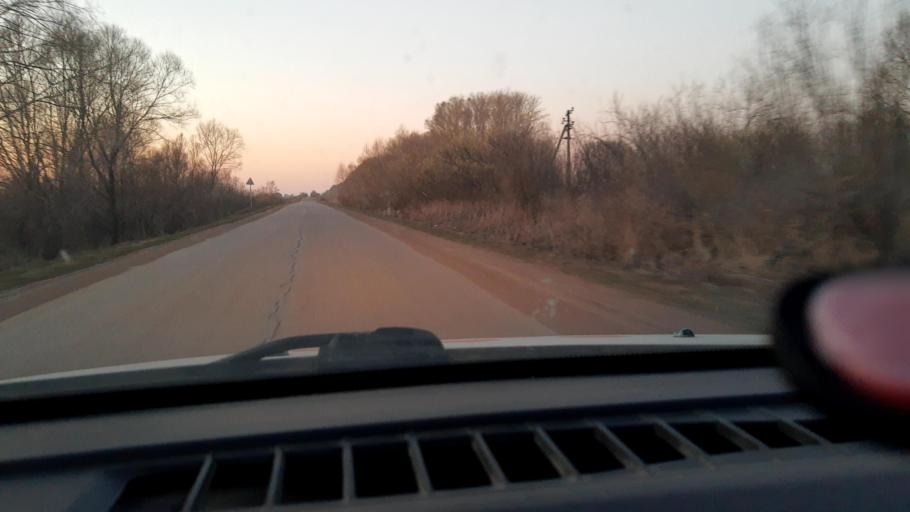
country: RU
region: Bashkortostan
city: Asanovo
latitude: 54.8502
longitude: 55.4559
